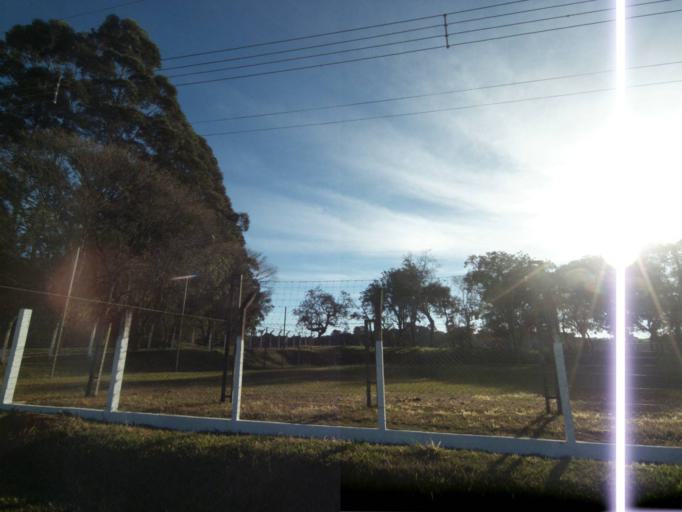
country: BR
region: Parana
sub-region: Tibagi
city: Tibagi
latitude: -24.5048
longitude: -50.4172
